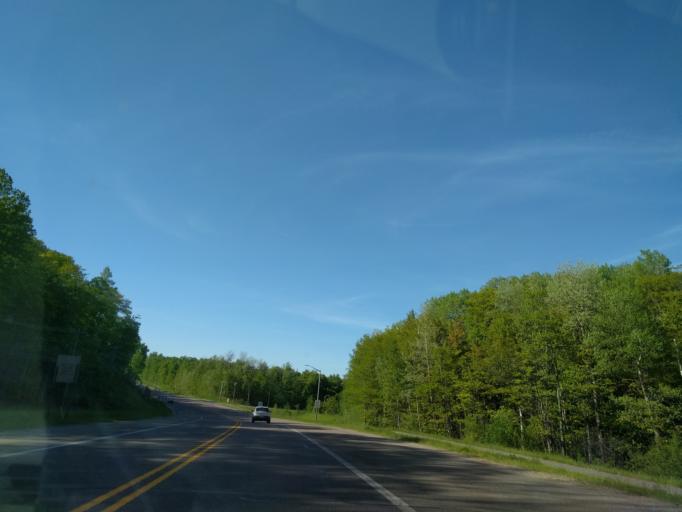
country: US
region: Michigan
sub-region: Marquette County
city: Marquette
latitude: 46.5145
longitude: -87.4132
